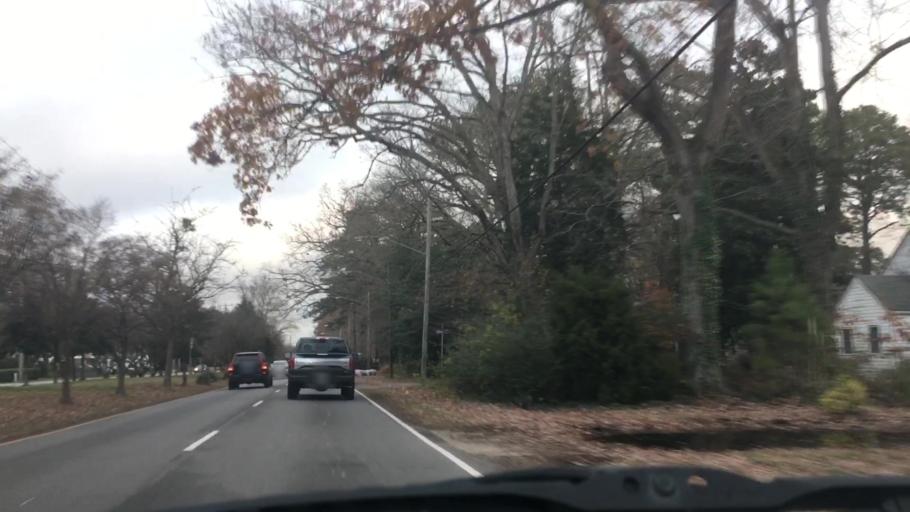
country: US
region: Virginia
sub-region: City of Norfolk
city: Norfolk
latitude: 36.9242
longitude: -76.2429
